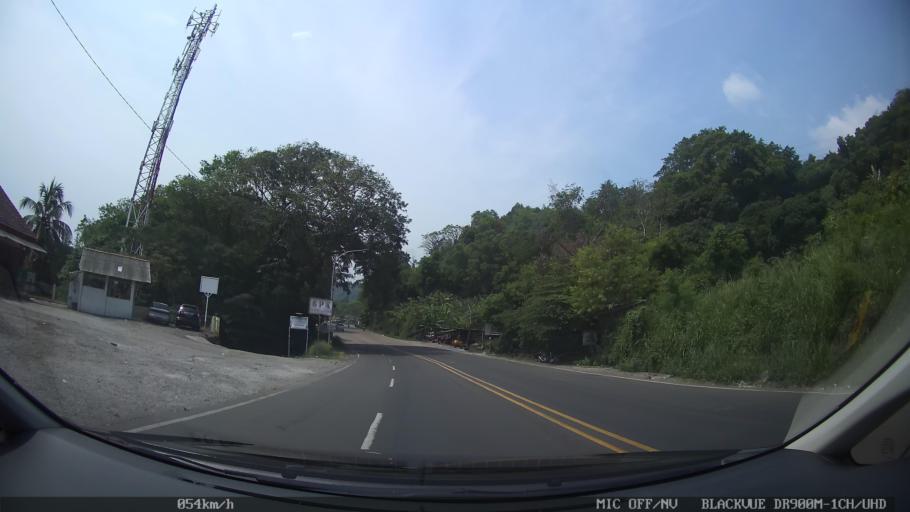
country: ID
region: Banten
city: Curug
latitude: -5.9482
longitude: 106.0035
